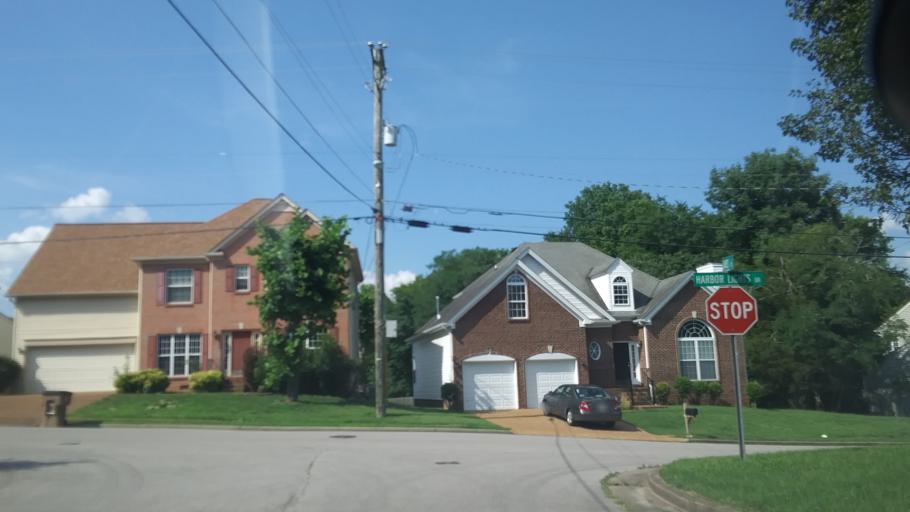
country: US
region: Tennessee
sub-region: Rutherford County
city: La Vergne
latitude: 36.0944
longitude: -86.6286
